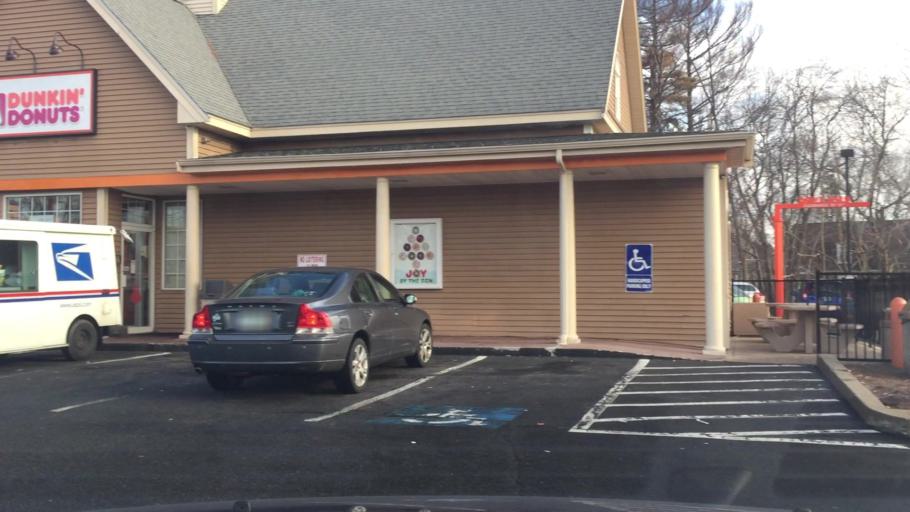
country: US
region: New Hampshire
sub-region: Rockingham County
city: Salem
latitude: 42.7805
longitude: -71.2282
